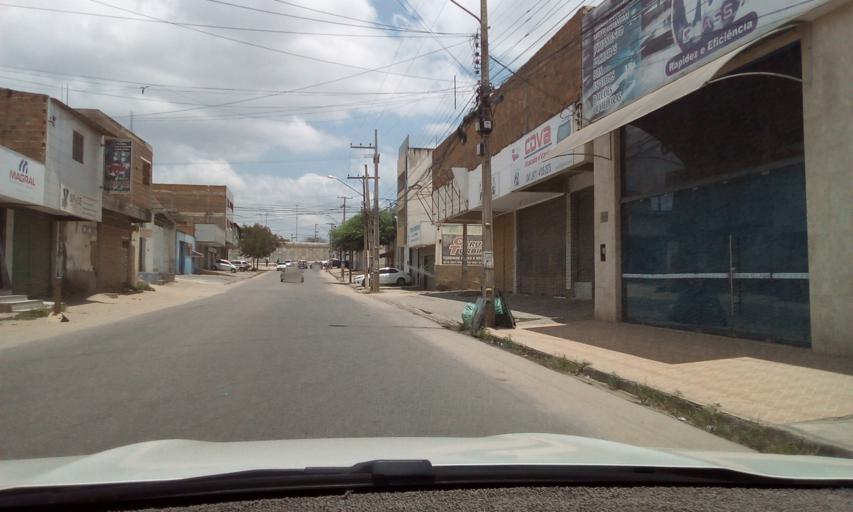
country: BR
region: Pernambuco
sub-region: Caruaru
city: Caruaru
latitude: -8.2724
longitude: -35.9835
